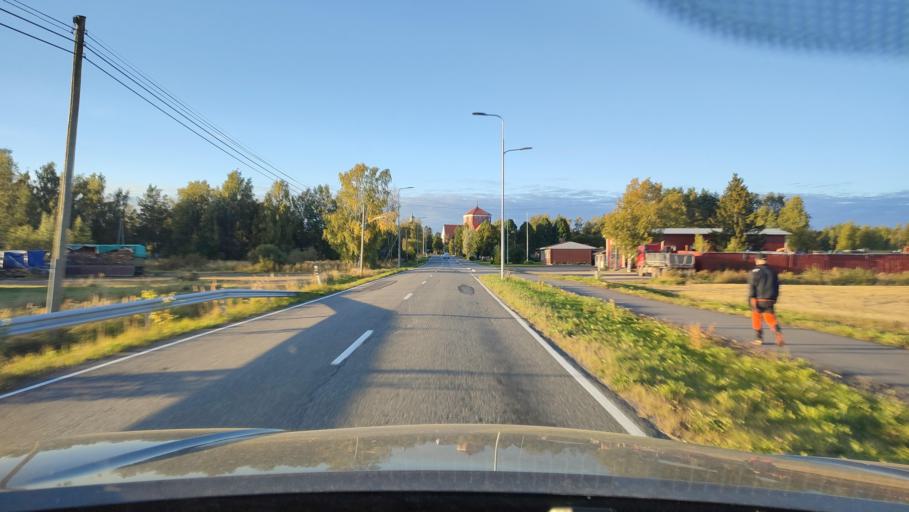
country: FI
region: Ostrobothnia
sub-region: Sydosterbotten
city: Kristinestad
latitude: 62.2425
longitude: 21.5210
